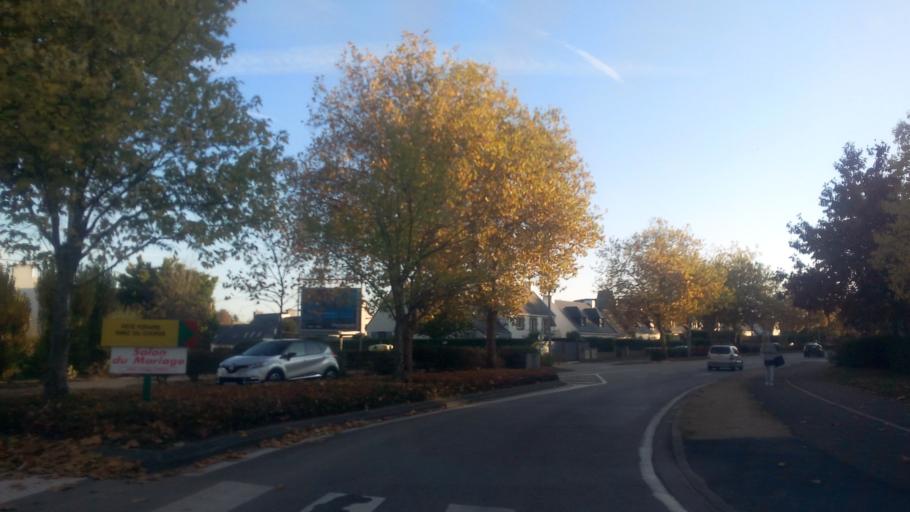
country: FR
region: Brittany
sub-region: Departement du Morbihan
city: Vannes
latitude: 47.6594
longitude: -2.7812
